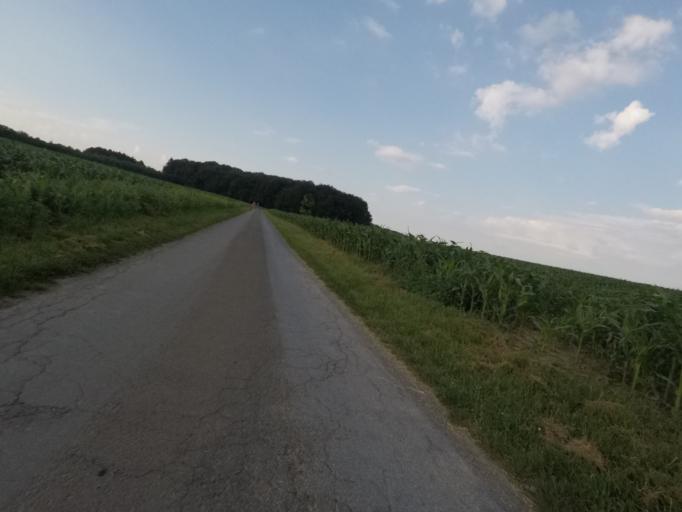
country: DE
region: North Rhine-Westphalia
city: Enger
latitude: 52.1275
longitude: 8.5693
